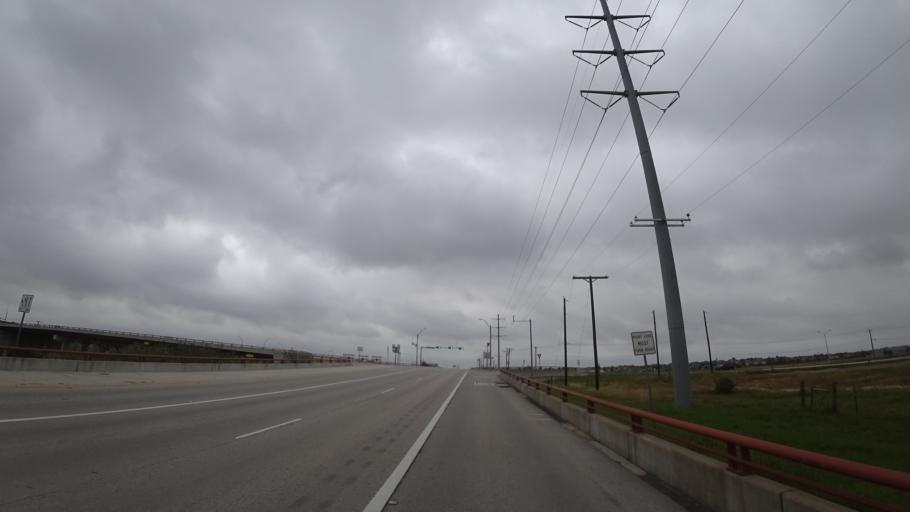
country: US
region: Texas
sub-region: Travis County
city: Windemere
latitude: 30.4834
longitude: -97.6151
